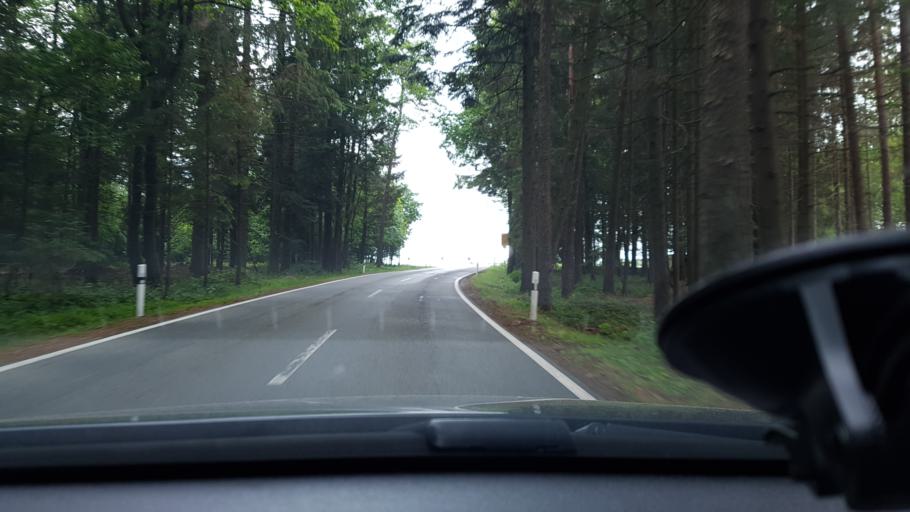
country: DE
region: Bavaria
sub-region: Lower Bavaria
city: Stubenberg
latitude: 48.3399
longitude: 13.0511
